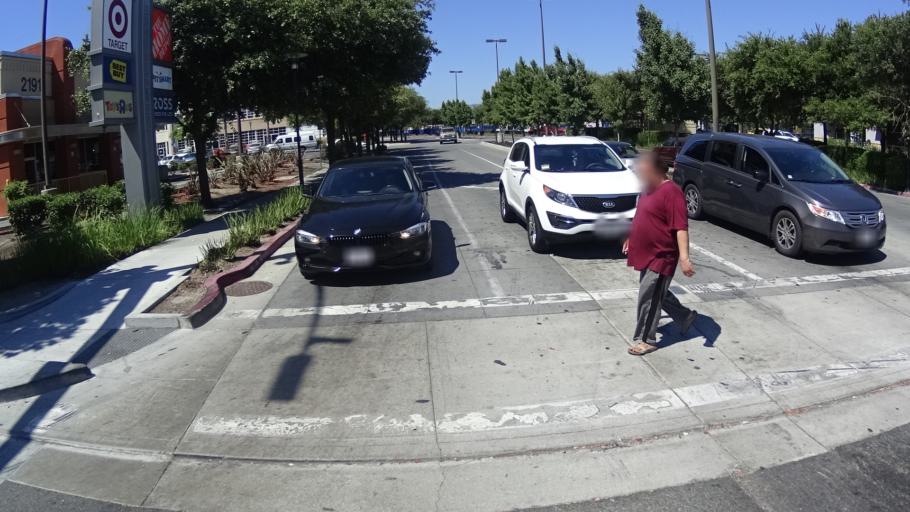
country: US
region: California
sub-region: Santa Clara County
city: Seven Trees
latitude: 37.3051
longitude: -121.8629
